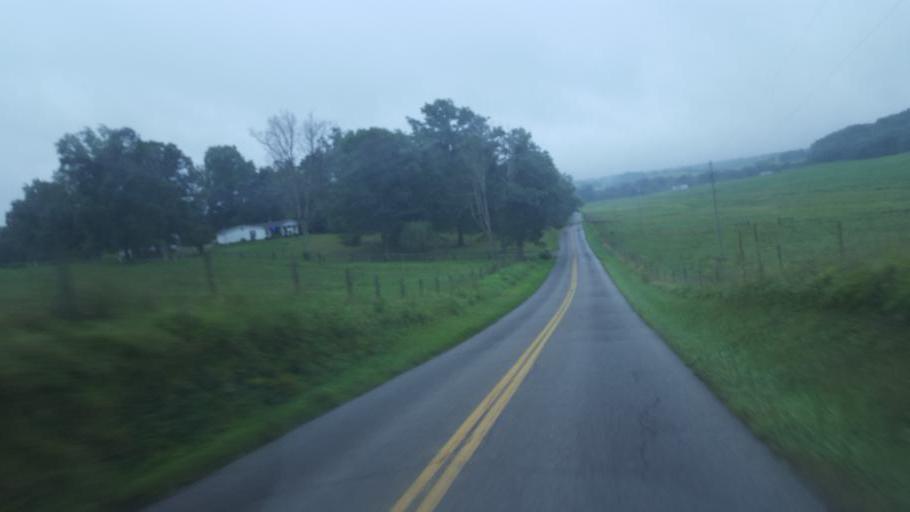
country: US
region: Ohio
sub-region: Jackson County
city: Oak Hill
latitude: 38.9360
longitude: -82.6038
